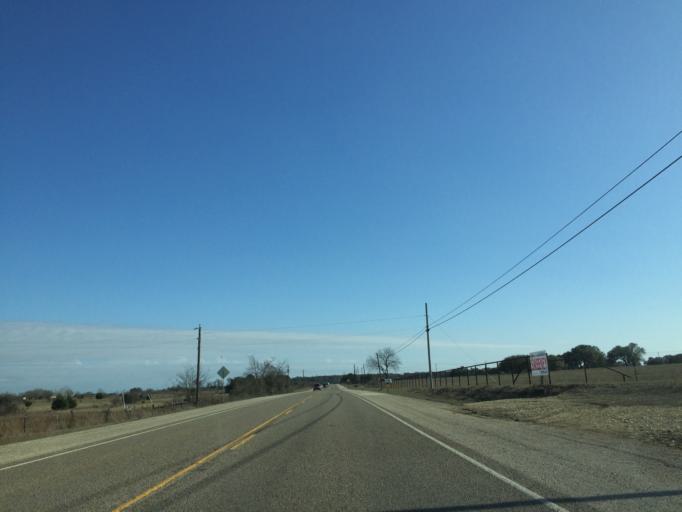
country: US
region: Texas
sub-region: Williamson County
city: Florence
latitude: 30.7787
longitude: -97.8510
